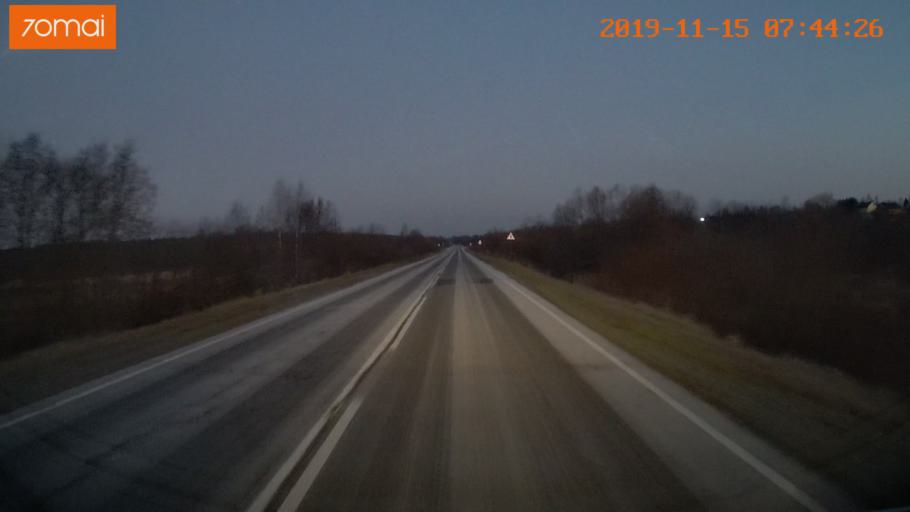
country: RU
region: Vologda
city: Sheksna
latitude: 58.8134
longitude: 38.3130
